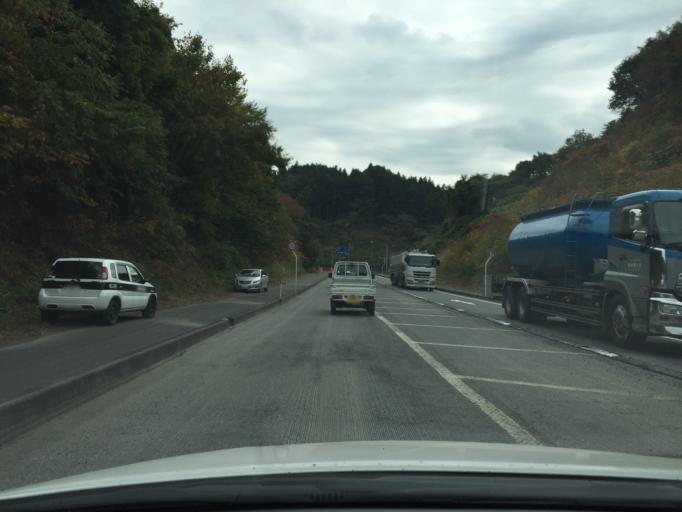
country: JP
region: Fukushima
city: Ishikawa
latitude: 37.0451
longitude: 140.3747
